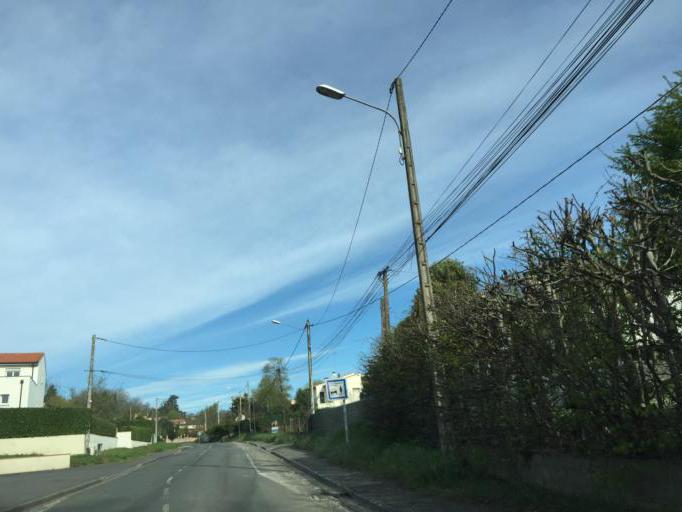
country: FR
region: Midi-Pyrenees
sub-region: Departement de la Haute-Garonne
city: Montastruc-la-Conseillere
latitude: 43.7183
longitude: 1.5963
